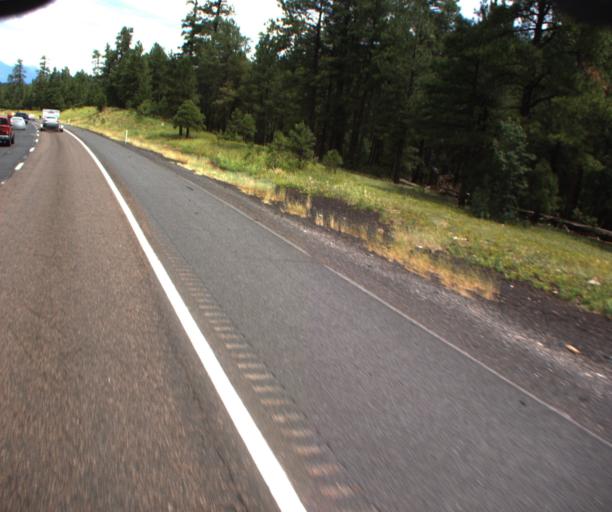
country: US
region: Arizona
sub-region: Coconino County
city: Mountainaire
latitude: 35.0325
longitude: -111.6839
